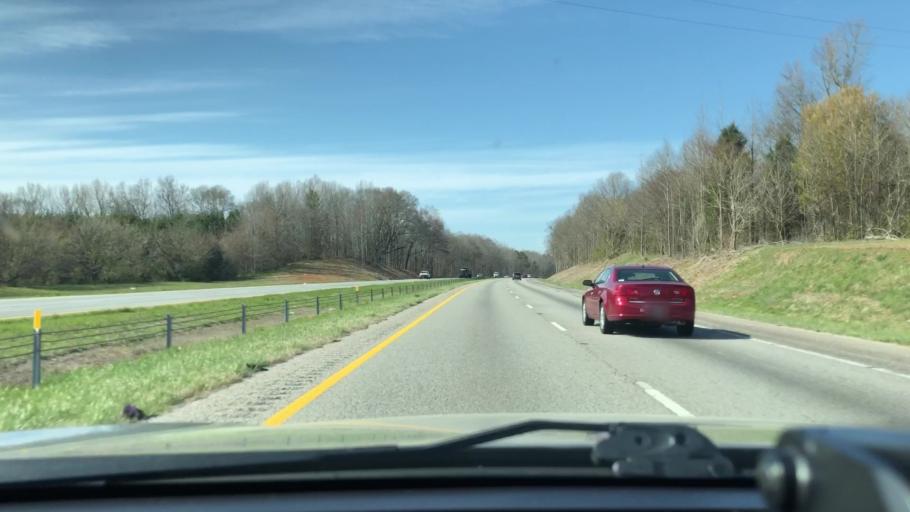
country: US
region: South Carolina
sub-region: Spartanburg County
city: Roebuck
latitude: 34.8671
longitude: -81.9862
